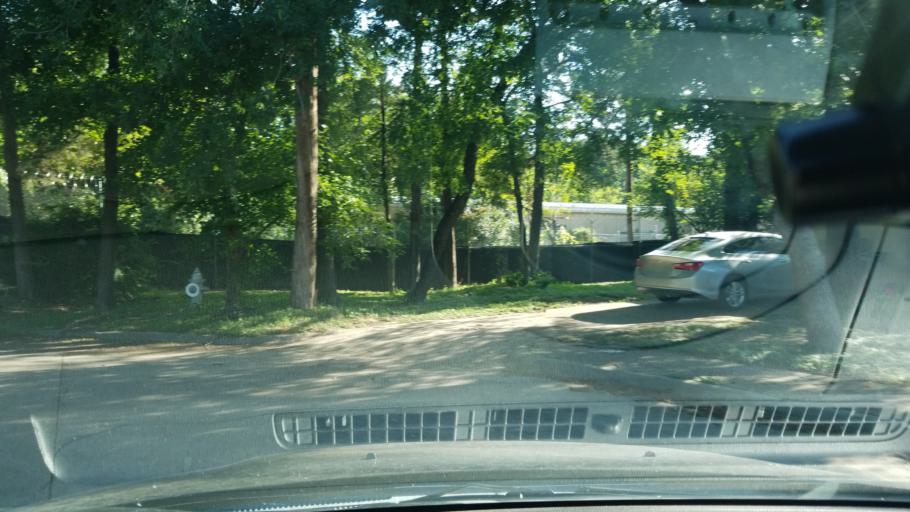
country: US
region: Texas
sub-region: Dallas County
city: Dallas
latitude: 32.7347
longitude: -96.8173
